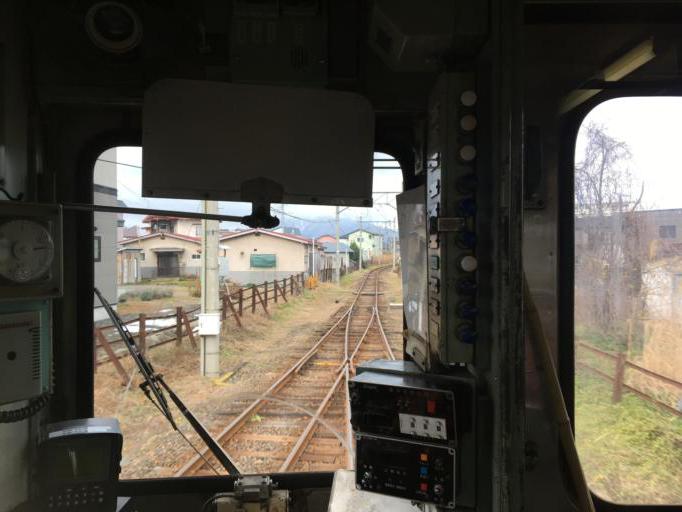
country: JP
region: Aomori
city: Hirosaki
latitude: 40.5677
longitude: 140.4798
